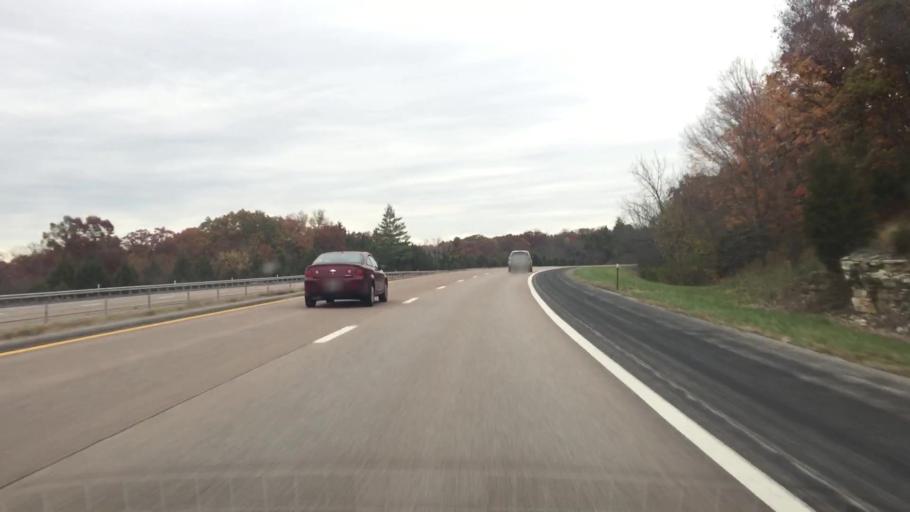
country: US
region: Missouri
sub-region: Boone County
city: Ashland
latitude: 38.6812
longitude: -92.2537
